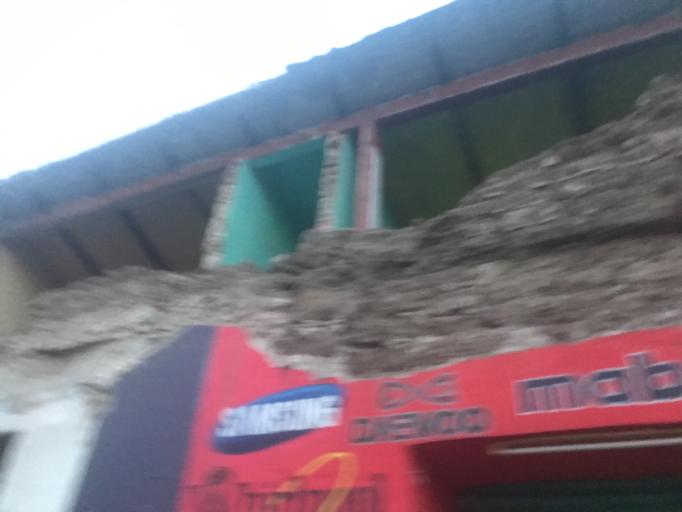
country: MX
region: Morelos
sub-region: Jojutla
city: Jojutla
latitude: 18.6132
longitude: -99.1815
